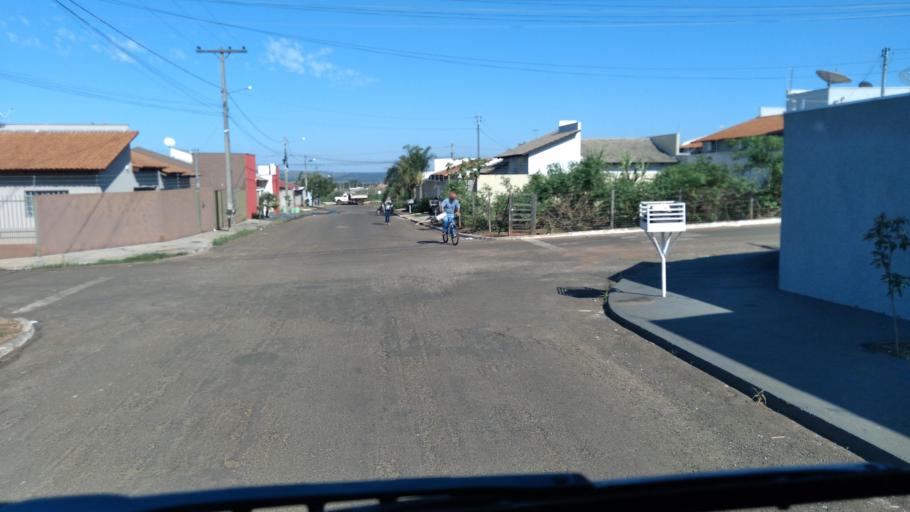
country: BR
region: Goias
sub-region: Mineiros
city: Mineiros
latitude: -17.5736
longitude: -52.5750
